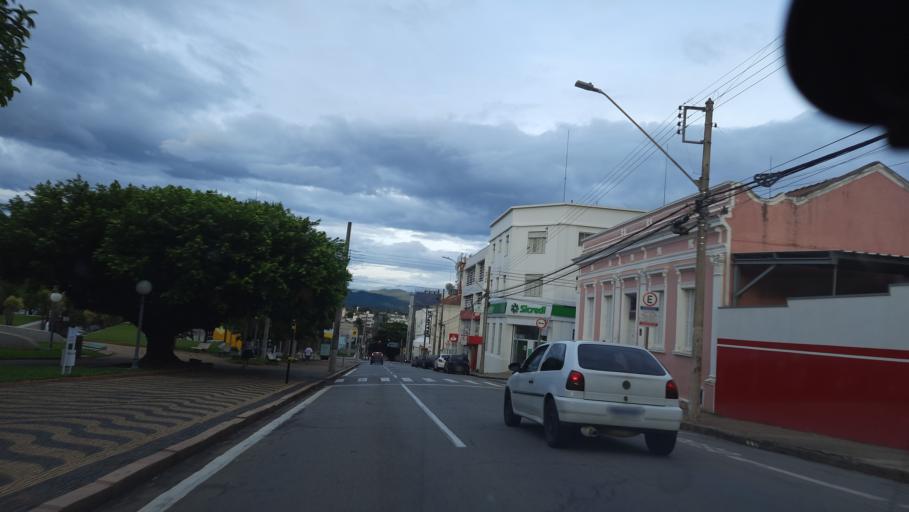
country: BR
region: Sao Paulo
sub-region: Sao Joao Da Boa Vista
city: Sao Joao da Boa Vista
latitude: -21.9692
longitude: -46.7975
